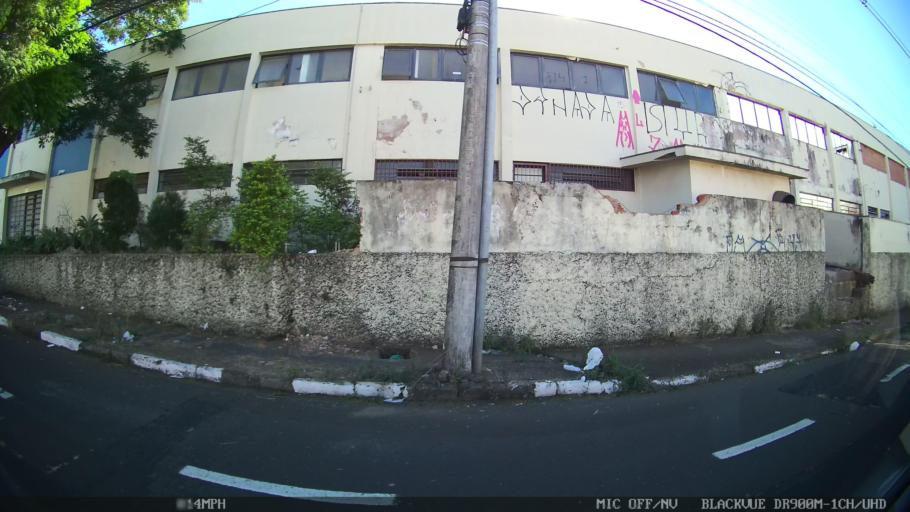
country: BR
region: Sao Paulo
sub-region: Franca
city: Franca
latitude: -20.5291
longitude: -47.4093
